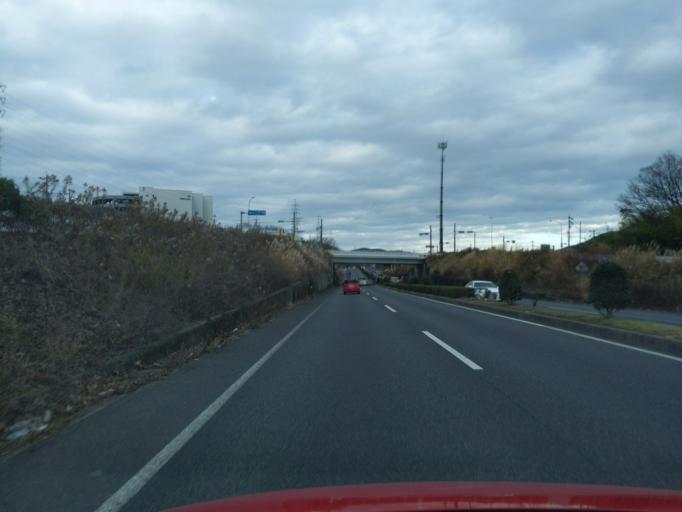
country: JP
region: Aichi
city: Kasugai
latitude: 35.3074
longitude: 137.0264
